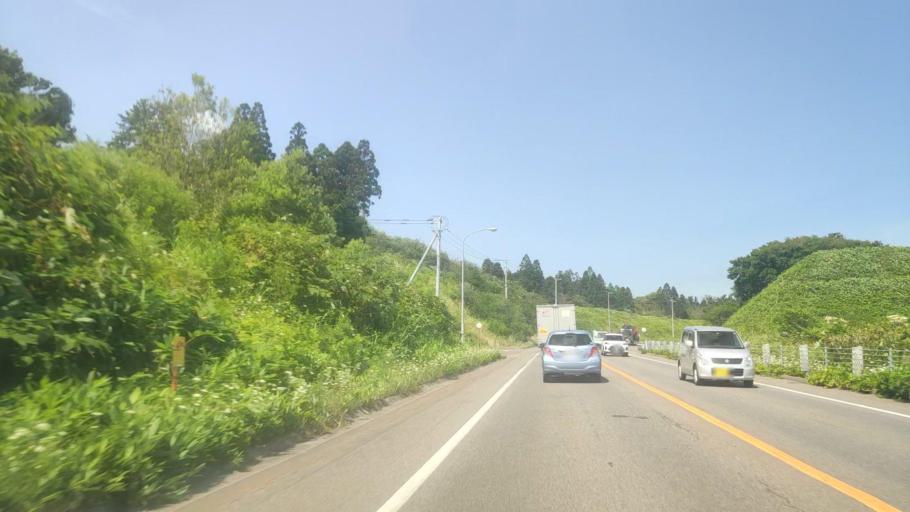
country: JP
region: Hokkaido
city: Nanae
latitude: 42.2005
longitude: 140.4099
